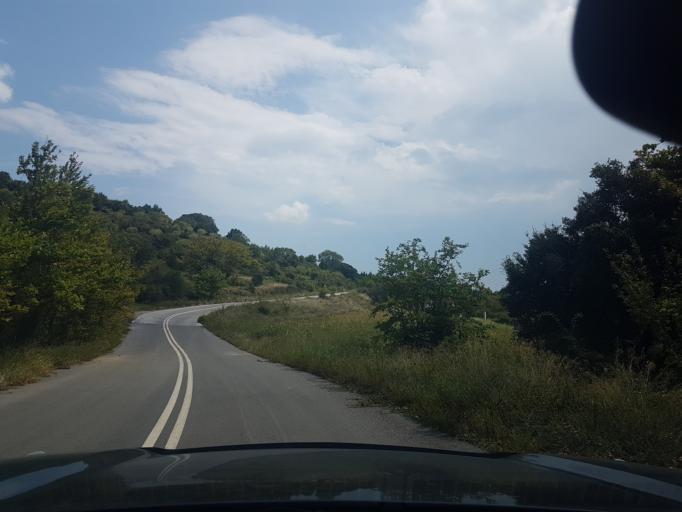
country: GR
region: Central Greece
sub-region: Nomos Evvoias
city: Kymi
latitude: 38.6488
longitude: 24.0342
